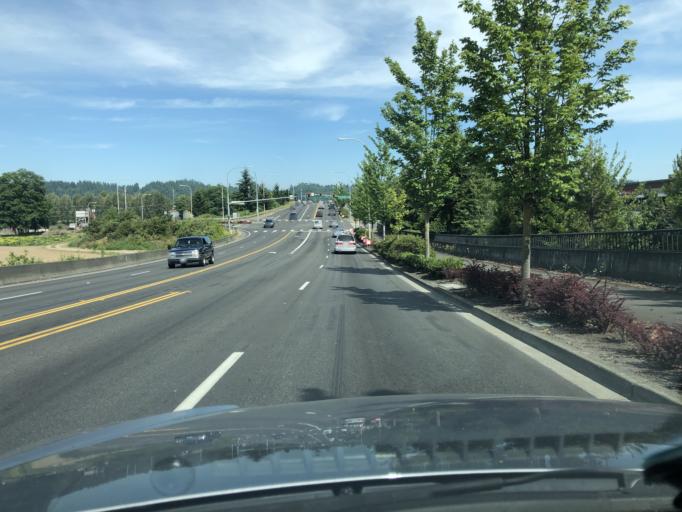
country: US
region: Washington
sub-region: King County
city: Kent
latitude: 47.3536
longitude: -122.2369
